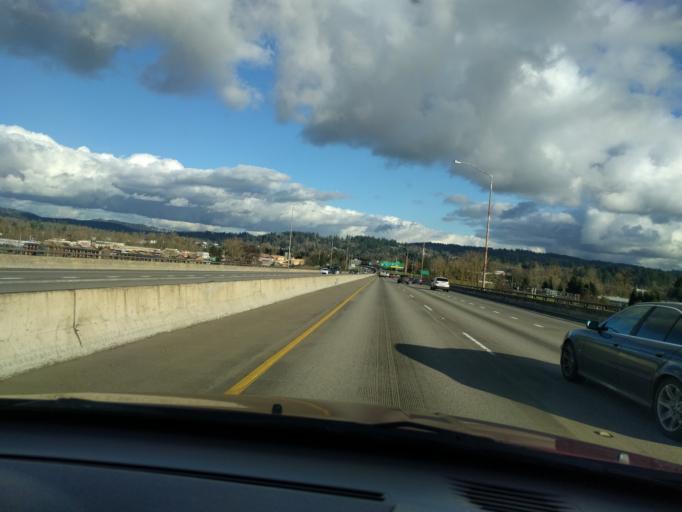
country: US
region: Oregon
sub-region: Clackamas County
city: Oregon City
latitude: 45.3641
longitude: -122.6052
